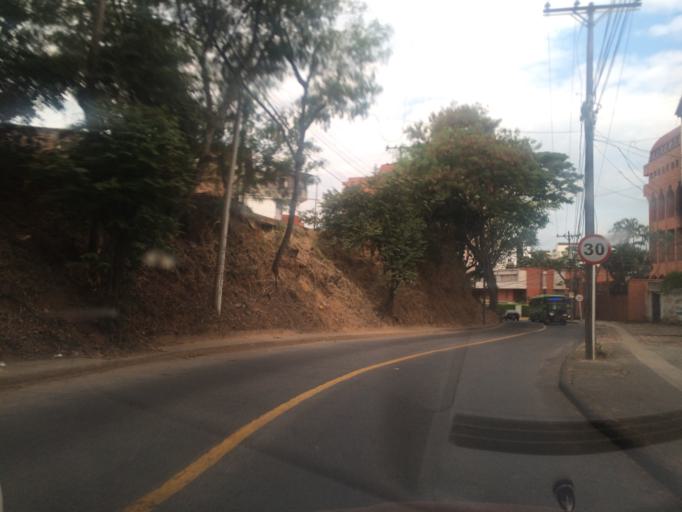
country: CO
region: Valle del Cauca
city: Cali
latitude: 3.4472
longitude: -76.5494
